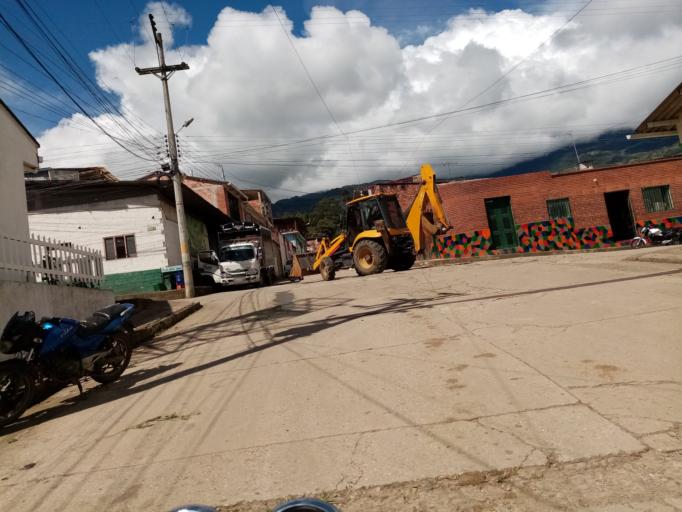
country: CO
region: Cundinamarca
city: Tenza
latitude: 5.0969
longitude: -73.4446
